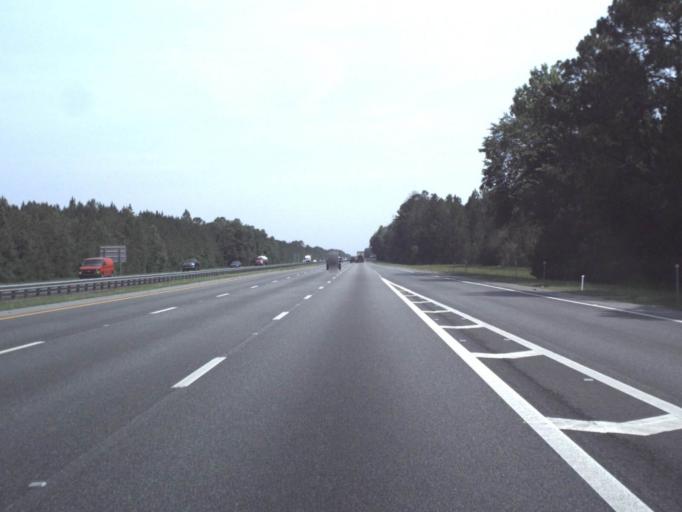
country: US
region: Florida
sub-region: Nassau County
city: Yulee
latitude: 30.6235
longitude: -81.6512
